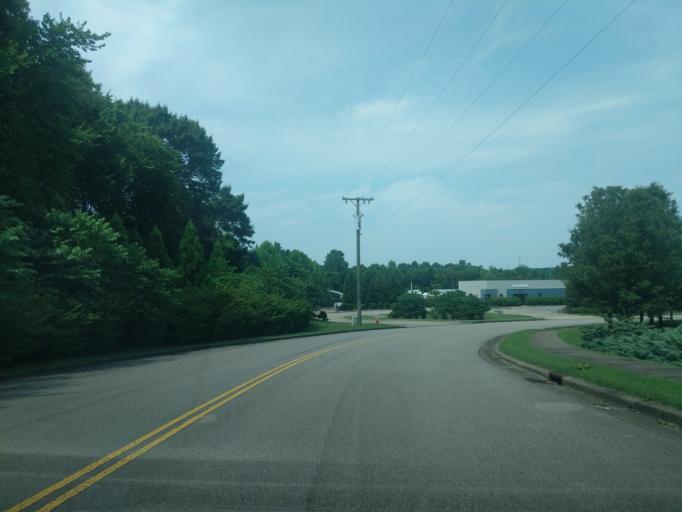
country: US
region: Tennessee
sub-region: Davidson County
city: Lakewood
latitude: 36.2644
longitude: -86.6667
